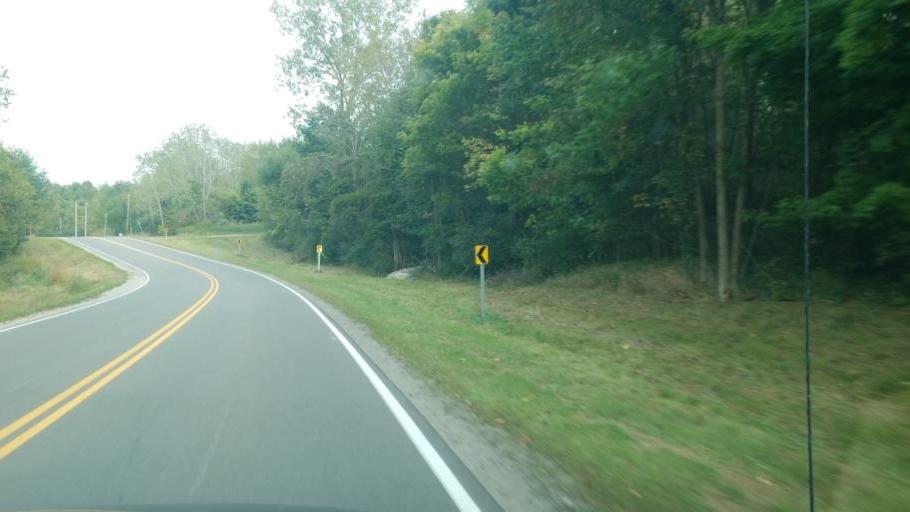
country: US
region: Ohio
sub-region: Crawford County
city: Galion
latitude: 40.7849
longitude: -82.8015
